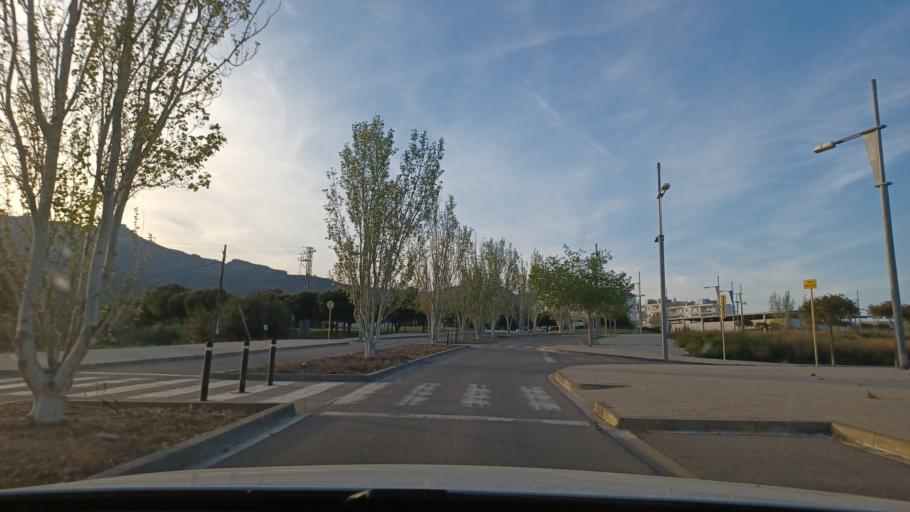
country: ES
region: Catalonia
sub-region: Provincia de Tarragona
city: Sant Carles de la Rapita
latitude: 40.6158
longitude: 0.5806
